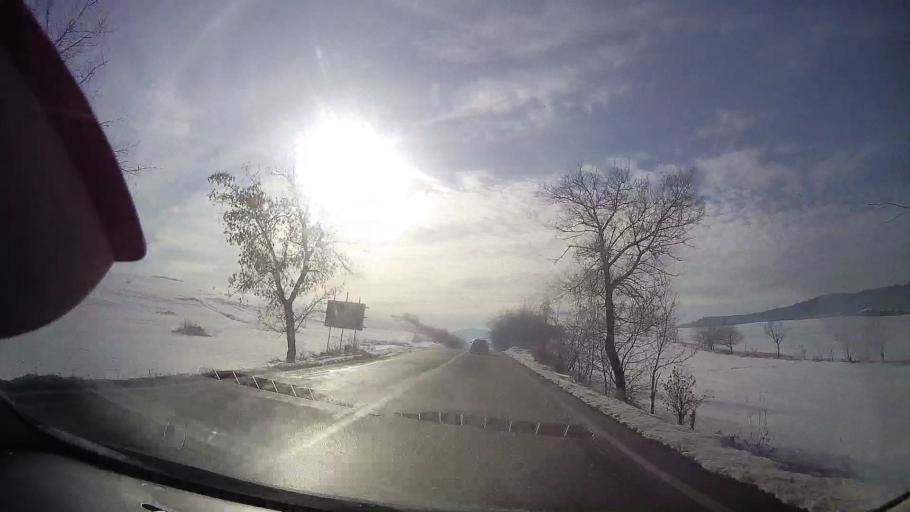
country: RO
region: Neamt
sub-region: Comuna Garcina
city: Garcina
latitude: 46.9970
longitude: 26.3672
